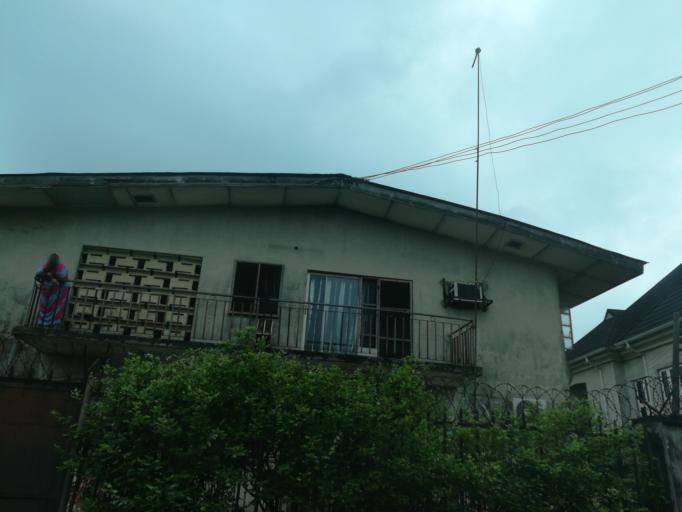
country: NG
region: Rivers
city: Port Harcourt
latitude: 4.8329
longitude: 7.0214
